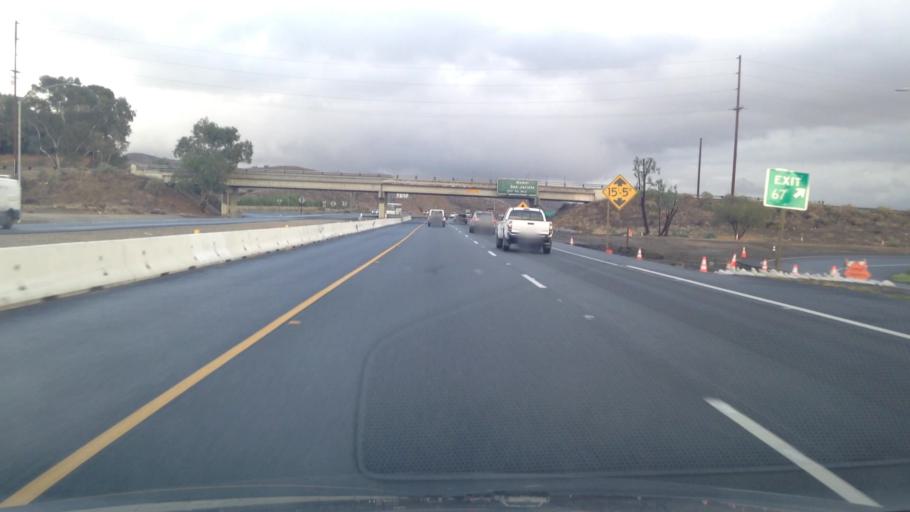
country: US
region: California
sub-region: Riverside County
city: Moreno Valley
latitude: 33.9392
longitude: -117.1411
